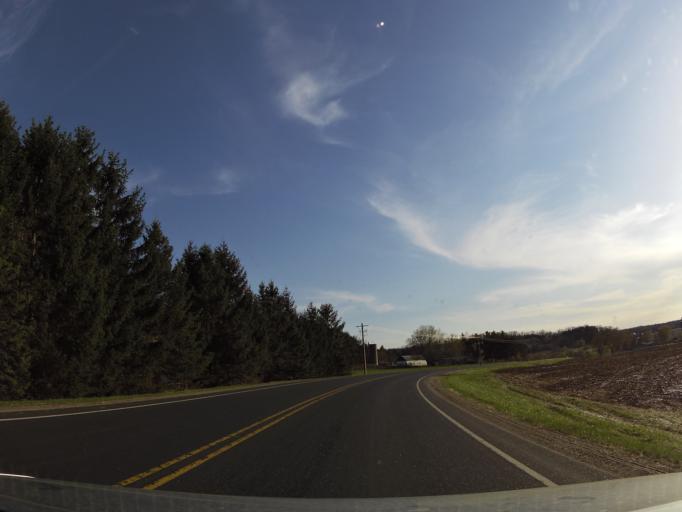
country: US
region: Wisconsin
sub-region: Pierce County
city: River Falls
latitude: 44.8316
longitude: -92.6608
